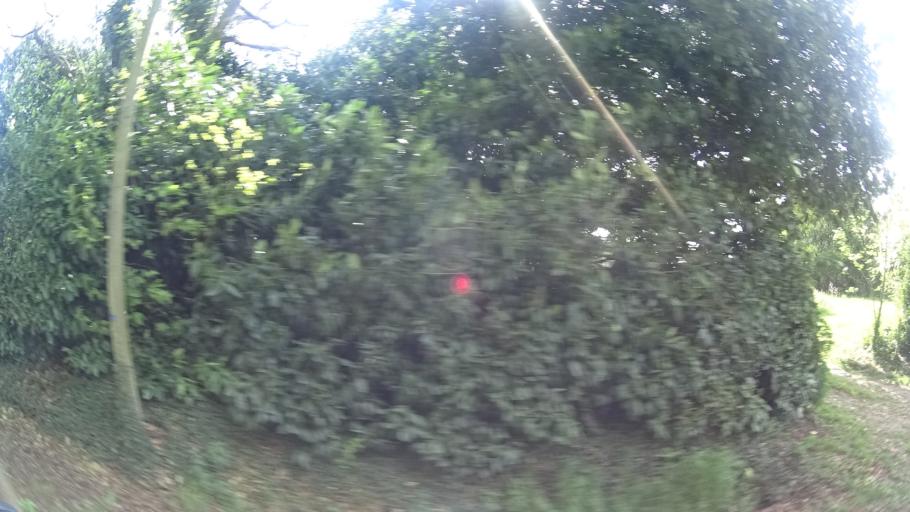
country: FR
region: Brittany
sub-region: Departement du Morbihan
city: Rieux
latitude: 47.5804
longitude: -2.1278
